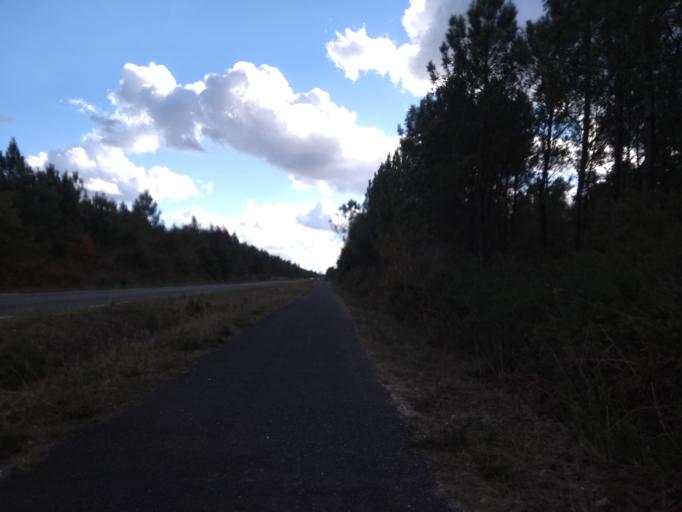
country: FR
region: Aquitaine
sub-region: Departement de la Gironde
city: Cestas
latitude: 44.7262
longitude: -0.6890
